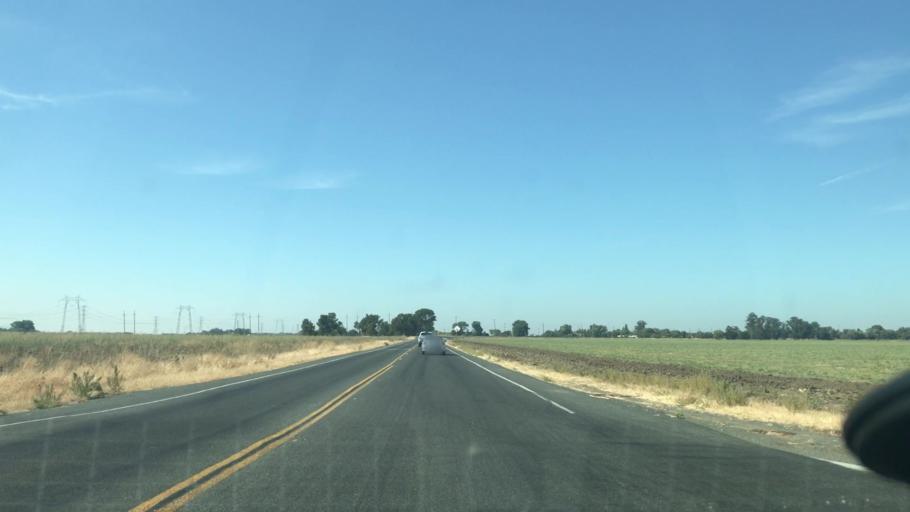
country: US
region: California
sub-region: Solano County
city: Vacaville
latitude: 38.3375
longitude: -121.9154
